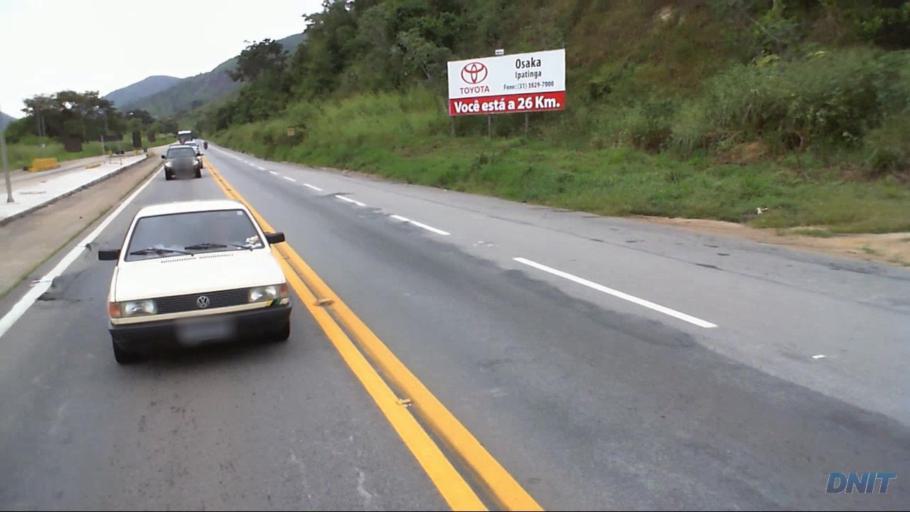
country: BR
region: Minas Gerais
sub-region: Timoteo
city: Timoteo
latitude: -19.5949
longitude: -42.7426
